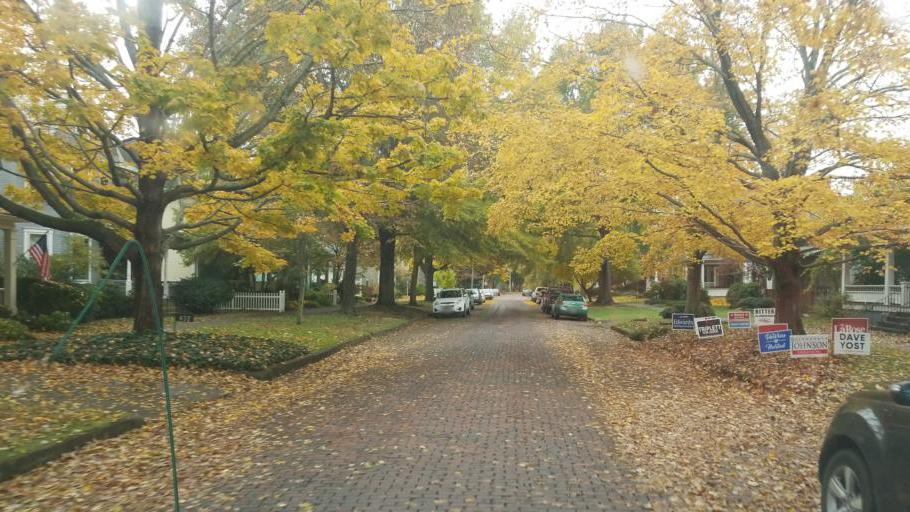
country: US
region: Ohio
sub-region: Washington County
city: Marietta
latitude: 39.4223
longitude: -81.4533
